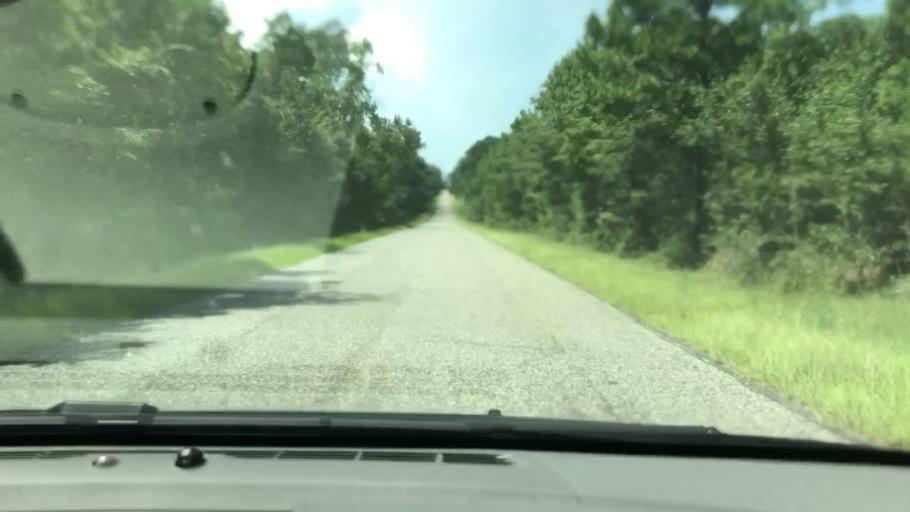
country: US
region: Georgia
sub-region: Seminole County
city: Donalsonville
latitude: 31.1598
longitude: -84.9959
